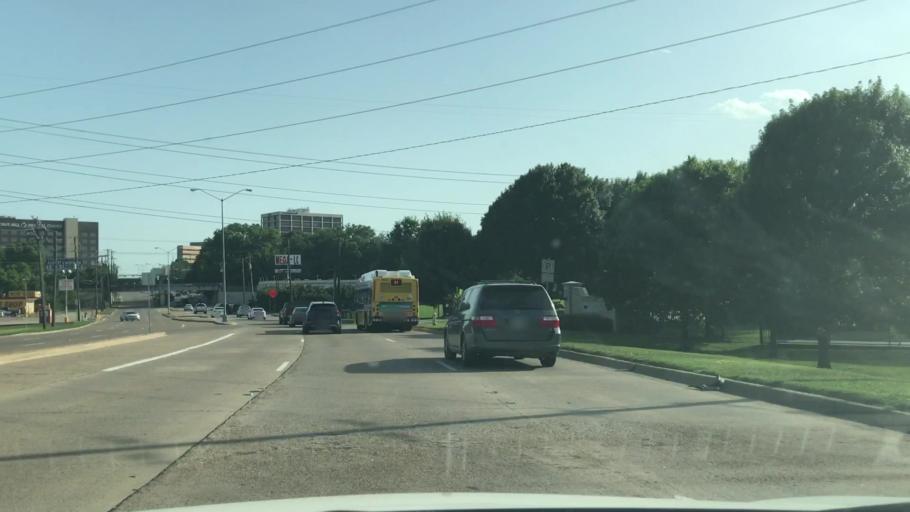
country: US
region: Texas
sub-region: Dallas County
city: University Park
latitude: 32.8885
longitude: -96.7571
